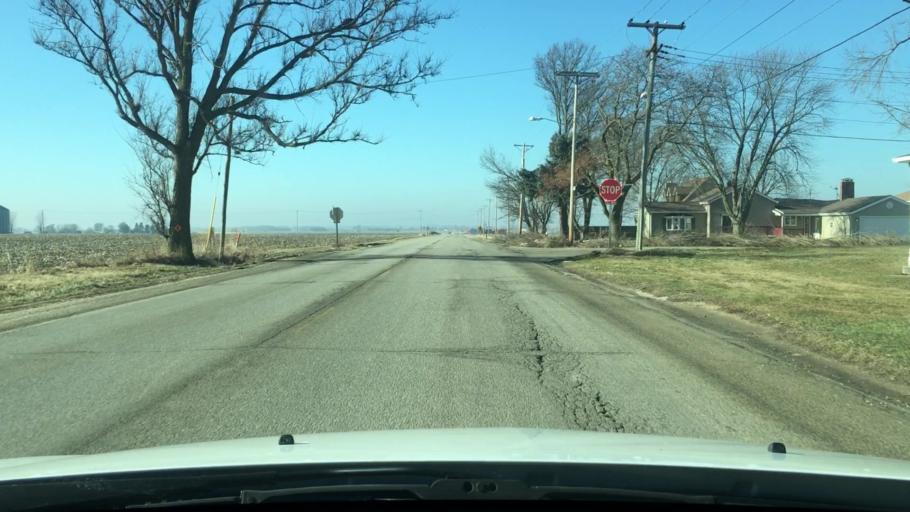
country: US
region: Illinois
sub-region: Ogle County
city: Rochelle
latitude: 41.8979
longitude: -89.0531
